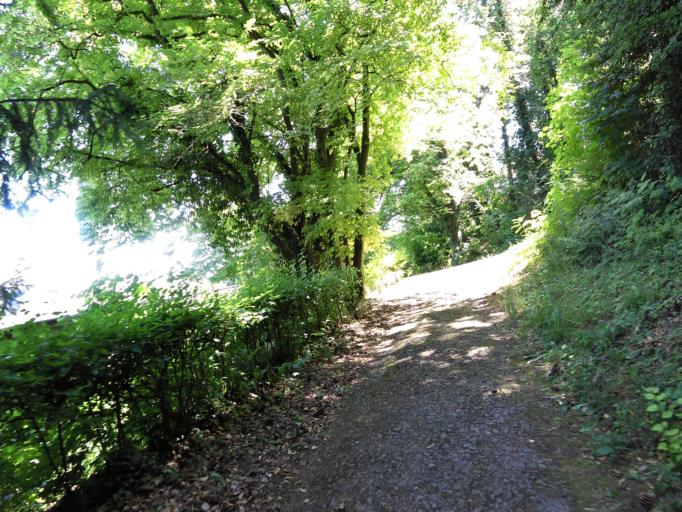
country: DE
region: Bavaria
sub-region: Regierungsbezirk Unterfranken
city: Wuerzburg
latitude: 49.7843
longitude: 9.9209
